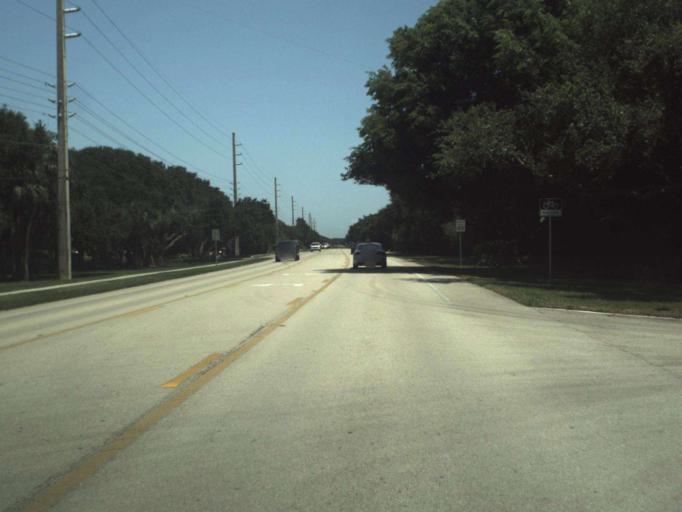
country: US
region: Florida
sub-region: Indian River County
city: Indian River Shores
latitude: 27.6857
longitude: -80.3683
